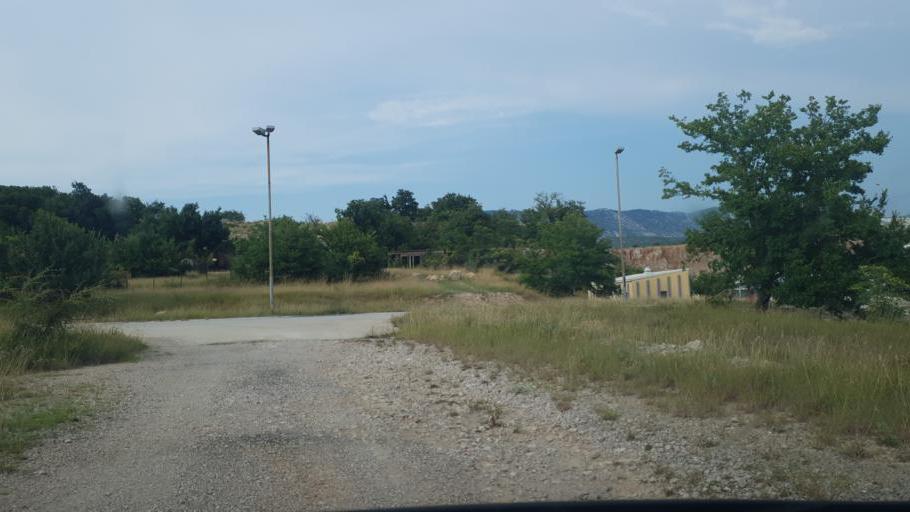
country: HR
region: Primorsko-Goranska
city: Omisalj
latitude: 45.2335
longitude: 14.5804
